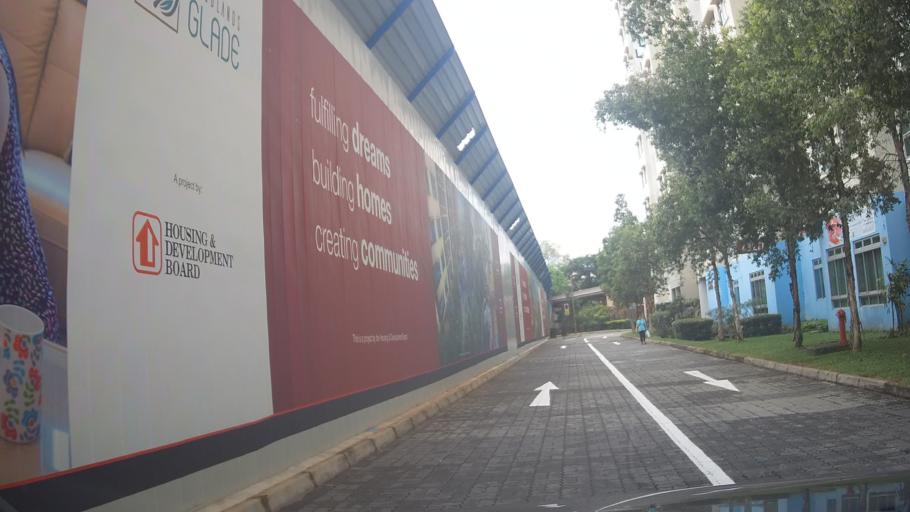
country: MY
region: Johor
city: Johor Bahru
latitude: 1.4480
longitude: 103.8023
